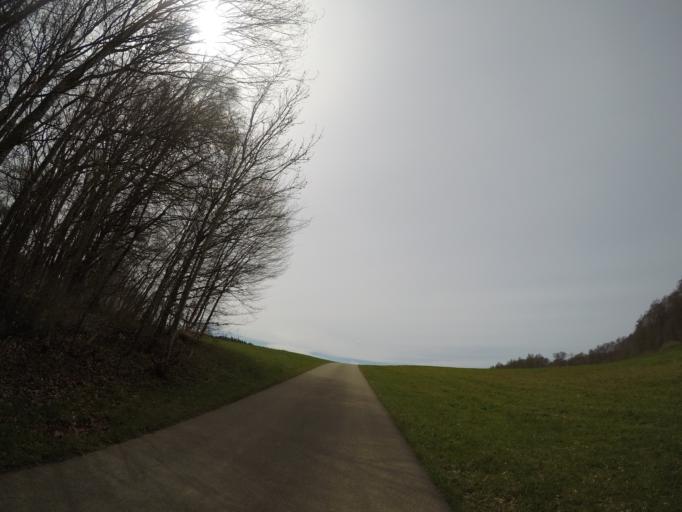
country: DE
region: Baden-Wuerttemberg
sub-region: Regierungsbezirk Stuttgart
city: Neidlingen
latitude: 48.5393
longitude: 9.5558
